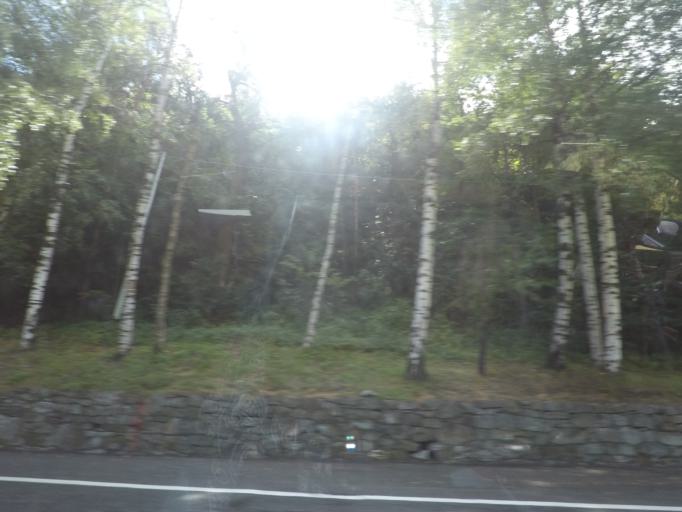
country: IT
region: Aosta Valley
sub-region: Valle d'Aosta
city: Antey-Saint-Andre
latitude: 45.7766
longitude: 7.5923
